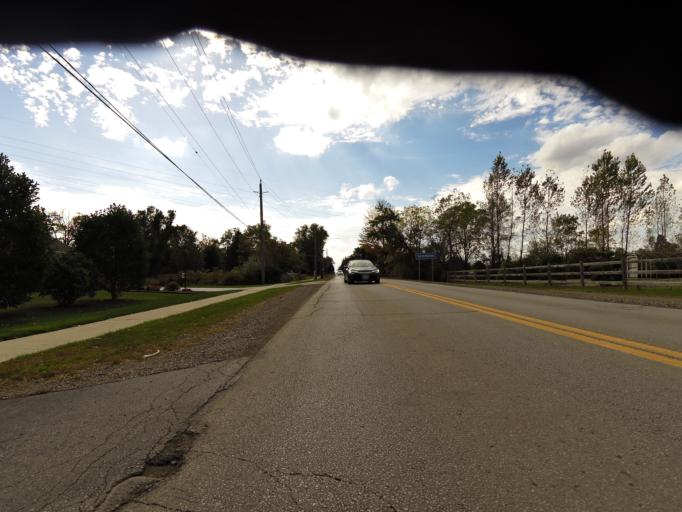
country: CA
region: Ontario
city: Burlington
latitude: 43.3438
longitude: -79.8954
